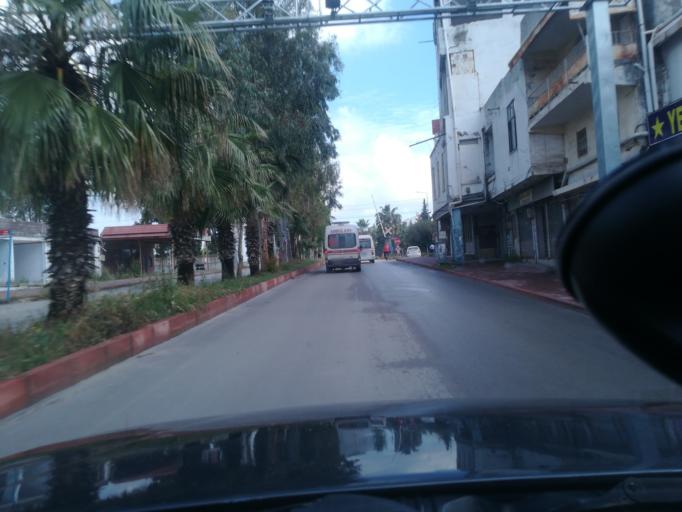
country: TR
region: Adana
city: Yuregir
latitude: 36.9840
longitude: 35.4307
